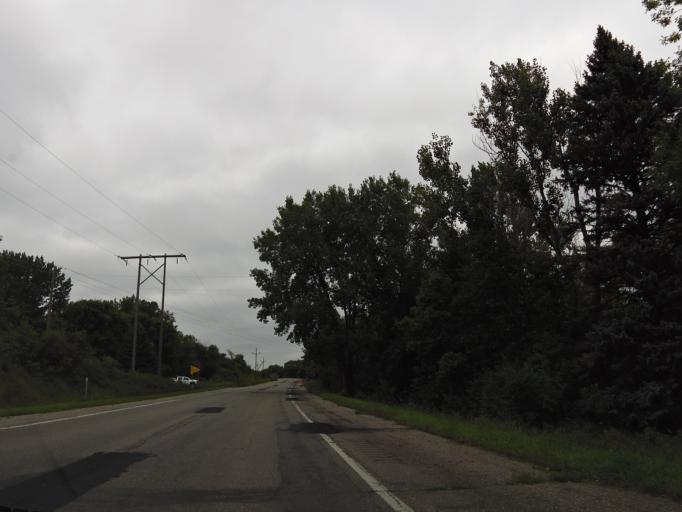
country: US
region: Minnesota
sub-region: Yellow Medicine County
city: Granite Falls
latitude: 44.8273
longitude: -95.6000
